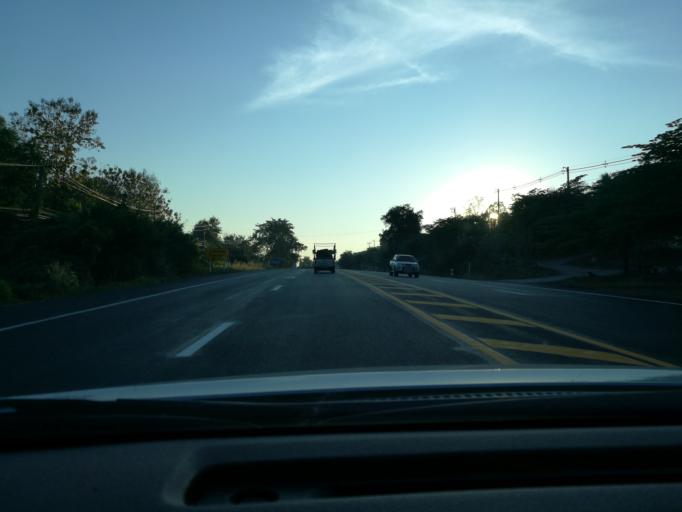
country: TH
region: Phitsanulok
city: Wang Thong
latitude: 16.8632
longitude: 100.4829
